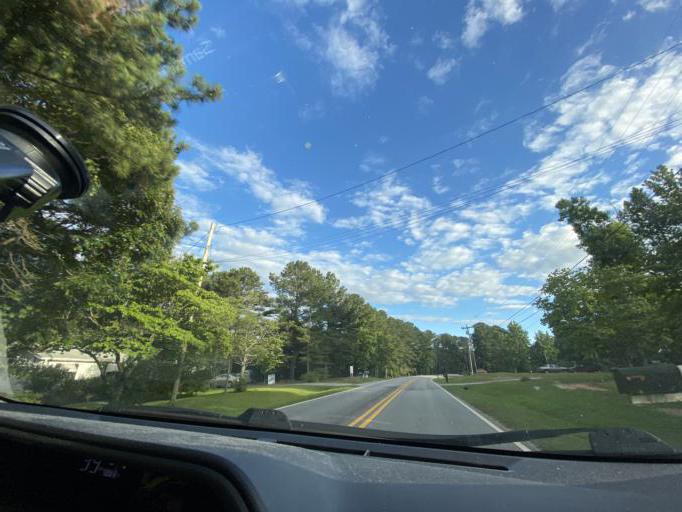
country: US
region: Georgia
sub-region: Fayette County
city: Peachtree City
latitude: 33.4310
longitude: -84.6482
